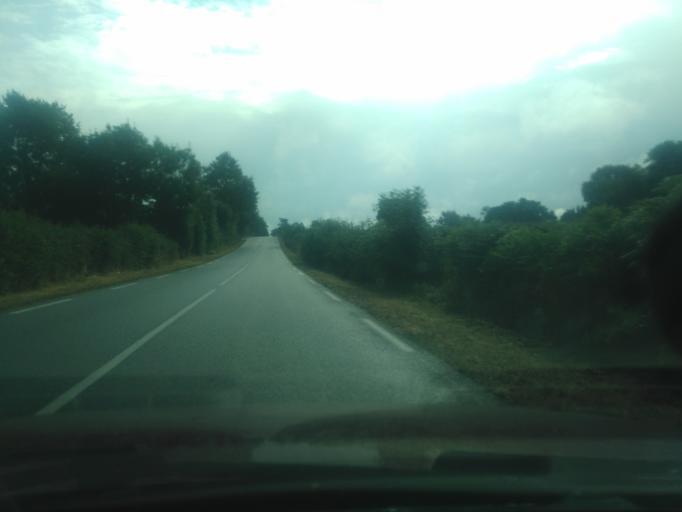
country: FR
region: Poitou-Charentes
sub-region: Departement des Deux-Sevres
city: Saint-Aubin-le-Cloud
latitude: 46.6217
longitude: -0.3622
